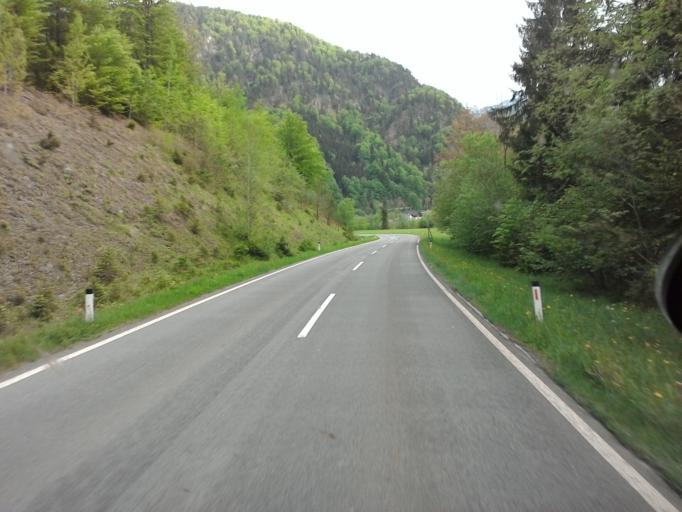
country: AT
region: Styria
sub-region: Politischer Bezirk Liezen
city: Altenmarkt bei Sankt Gallen
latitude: 47.7093
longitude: 14.6846
